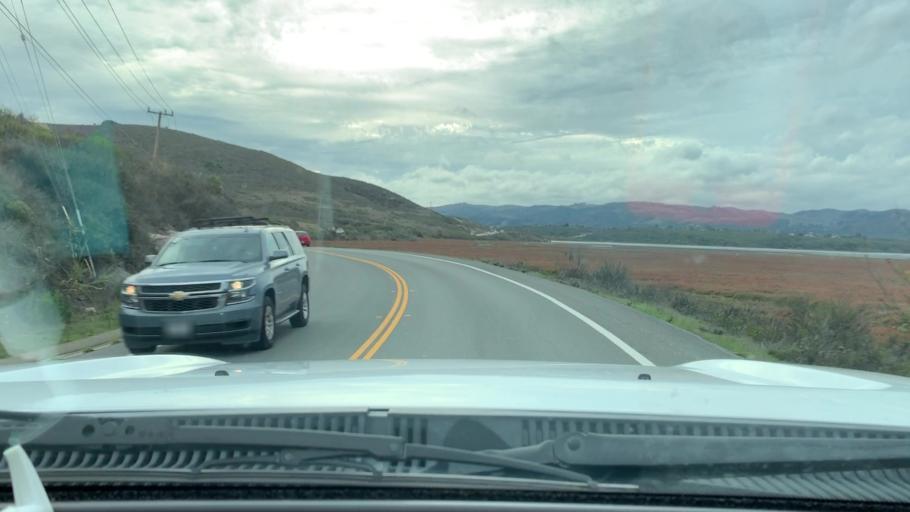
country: US
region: California
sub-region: San Luis Obispo County
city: Morro Bay
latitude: 35.3501
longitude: -120.8281
